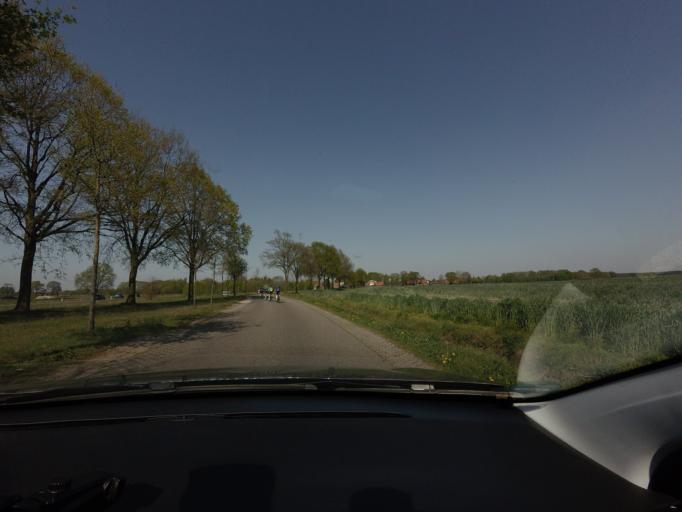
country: NL
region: North Brabant
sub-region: Gemeente Baarle-Nassau
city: Baarle-Nassau
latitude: 51.4778
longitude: 4.9674
